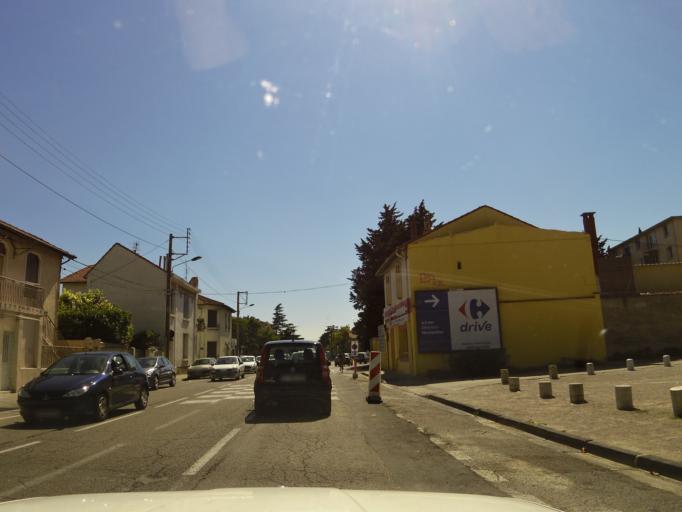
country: FR
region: Languedoc-Roussillon
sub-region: Departement du Gard
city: Nimes
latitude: 43.8279
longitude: 4.3738
